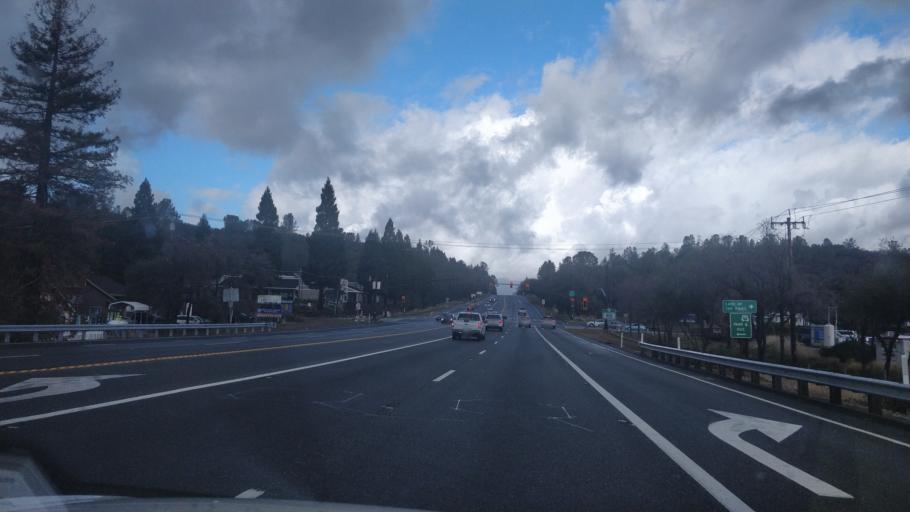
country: US
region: California
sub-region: Nevada County
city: Lake of the Pines
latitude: 39.0413
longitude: -121.0948
